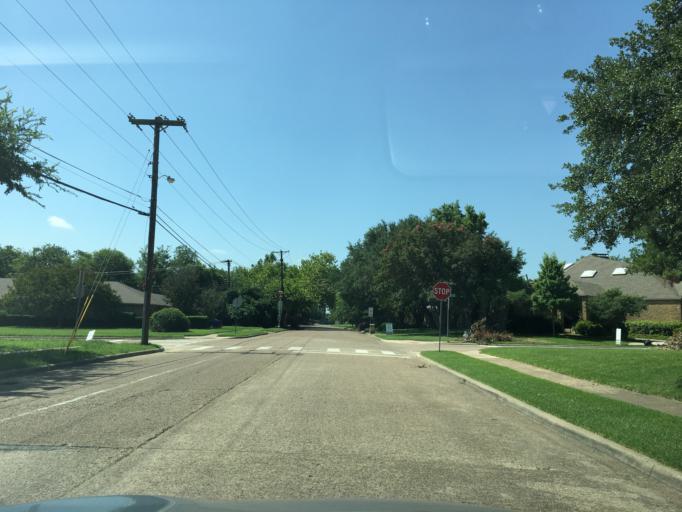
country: US
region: Texas
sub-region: Dallas County
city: University Park
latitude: 32.9014
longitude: -96.7843
